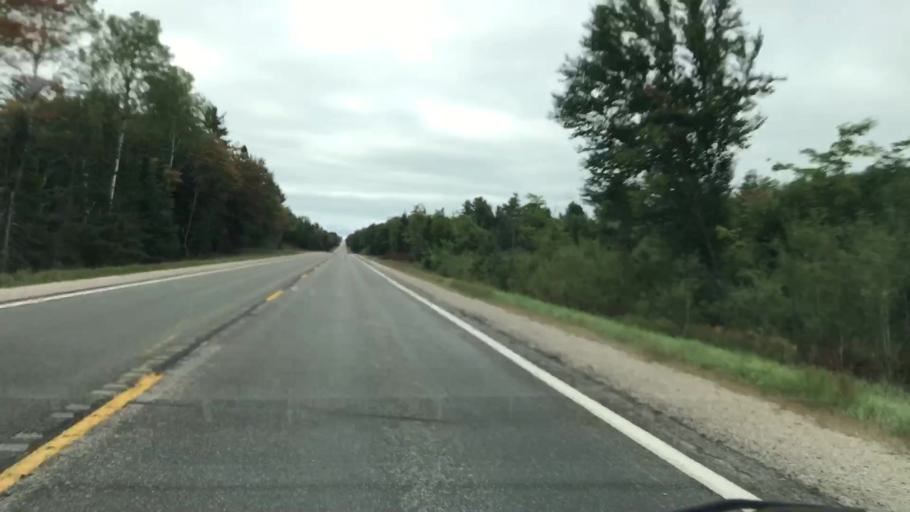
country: US
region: Michigan
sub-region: Luce County
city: Newberry
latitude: 46.2404
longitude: -85.5723
